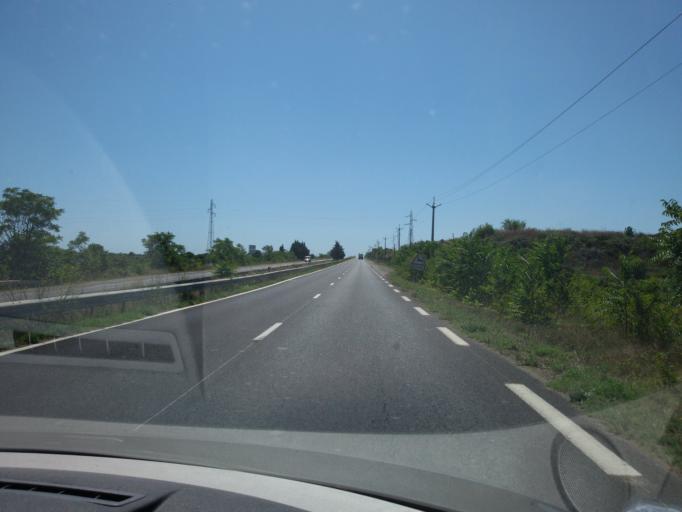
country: FR
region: Languedoc-Roussillon
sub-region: Departement de l'Herault
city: Saint-Jean-de-Vedas
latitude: 43.5417
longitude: 3.8228
